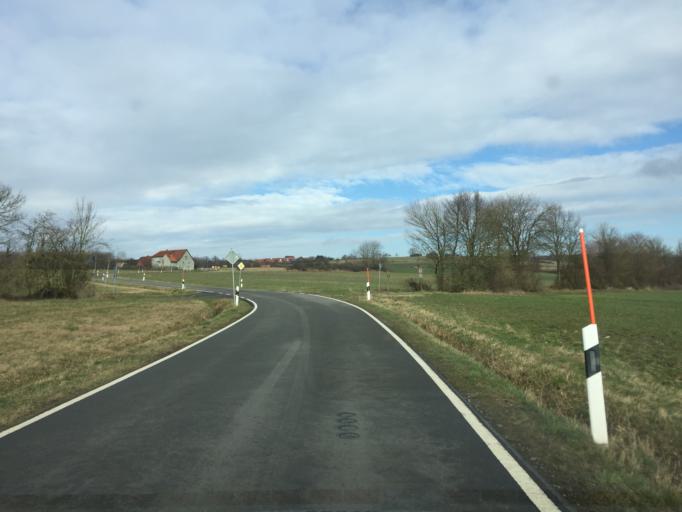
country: DE
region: Lower Saxony
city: Aerzen
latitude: 52.0997
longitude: 9.1613
